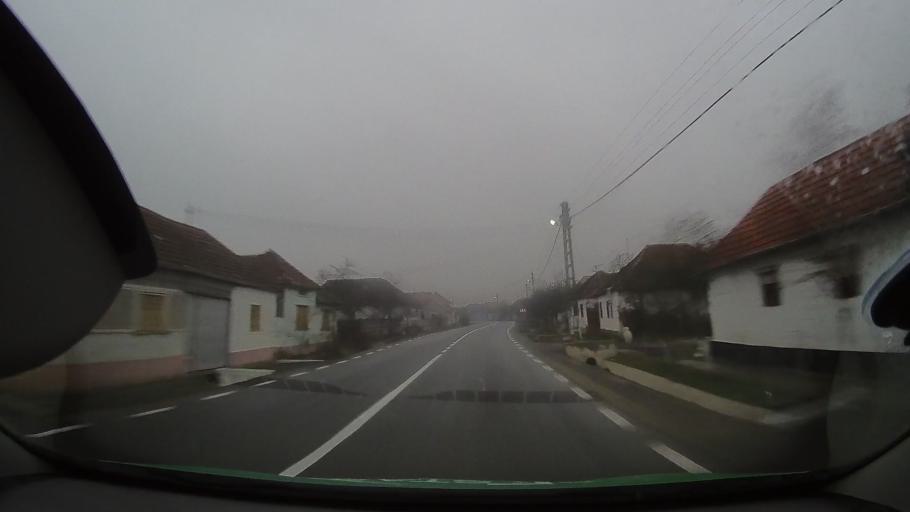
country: RO
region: Bihor
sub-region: Comuna Olcea
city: Calacea
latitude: 46.6434
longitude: 21.9560
